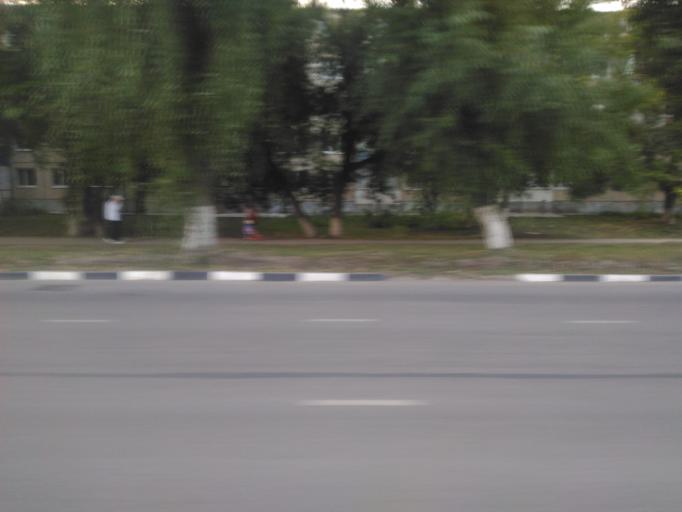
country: RU
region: Ulyanovsk
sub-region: Ulyanovskiy Rayon
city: Ulyanovsk
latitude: 54.2735
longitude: 48.2885
